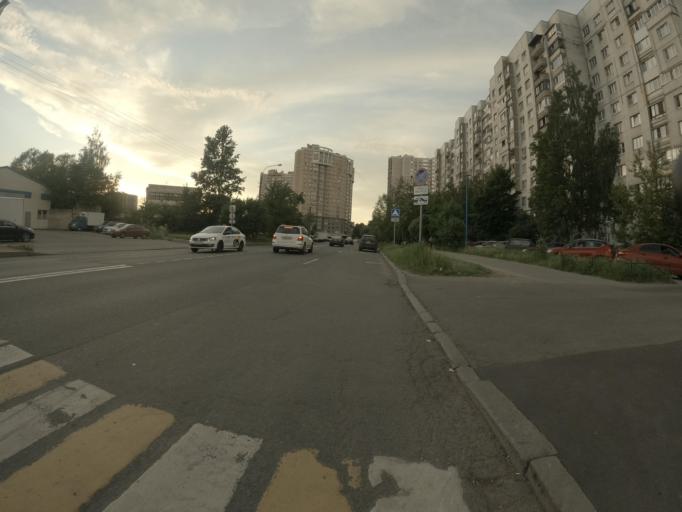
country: RU
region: St.-Petersburg
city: Kupchino
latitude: 59.8384
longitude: 30.3110
